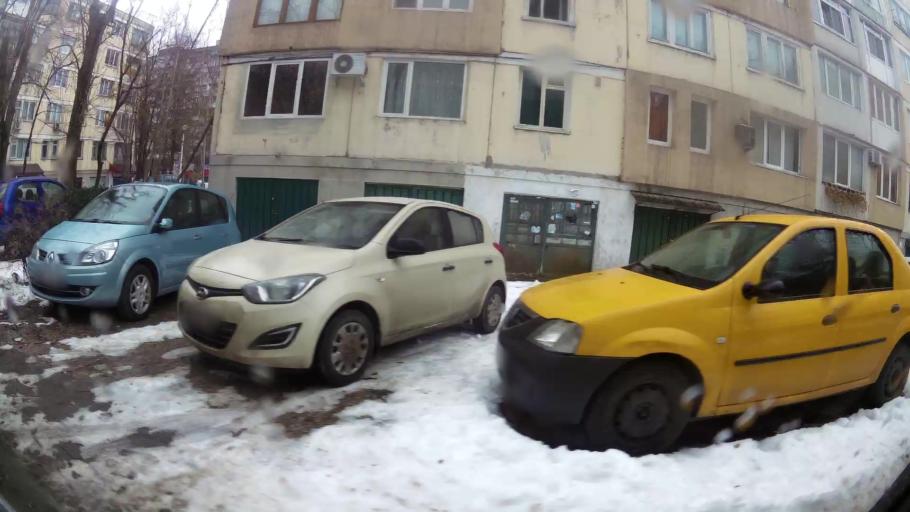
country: RO
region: Ilfov
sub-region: Comuna Chiajna
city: Rosu
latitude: 44.4163
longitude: 26.0163
